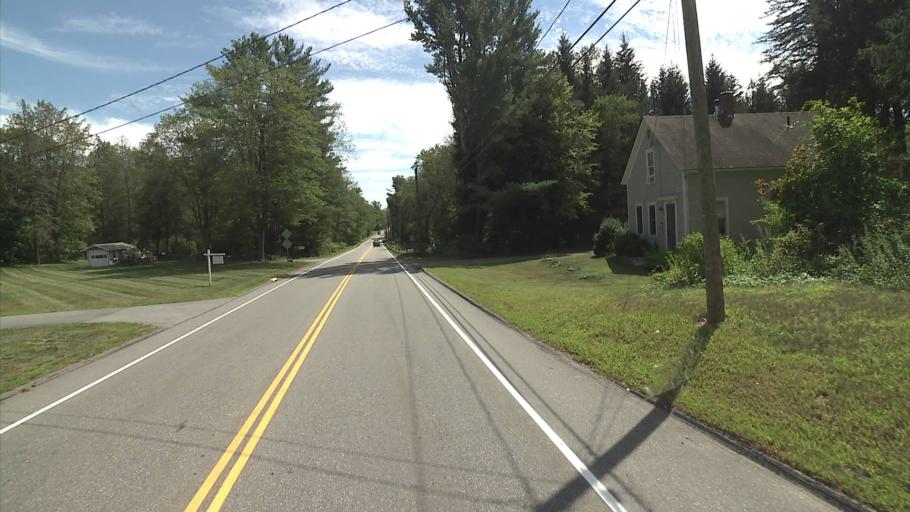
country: US
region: Connecticut
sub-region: Tolland County
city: Mansfield City
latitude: 41.7700
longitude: -72.2025
